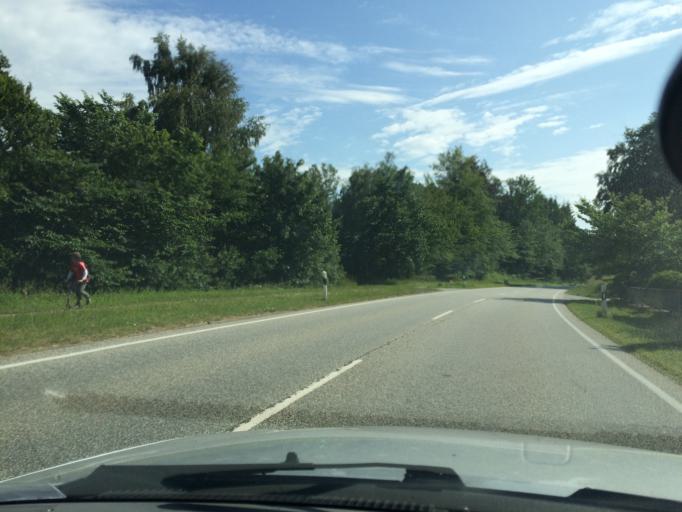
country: DE
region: Schleswig-Holstein
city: Oeversee
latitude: 54.7169
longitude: 9.4438
